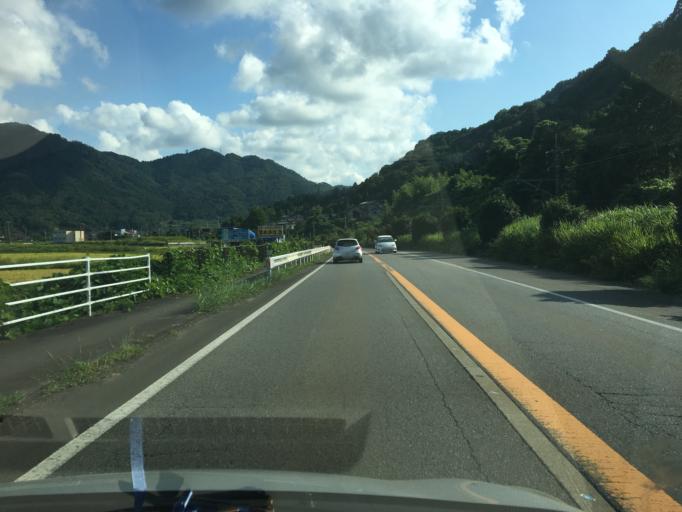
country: JP
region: Hyogo
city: Toyooka
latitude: 35.4297
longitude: 134.7875
